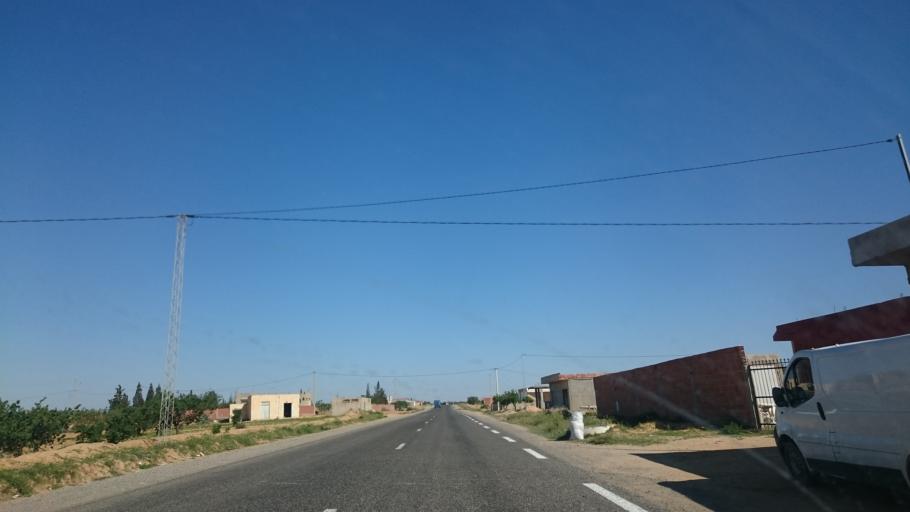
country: TN
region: Safaqis
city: Sfax
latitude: 34.7803
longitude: 10.5041
